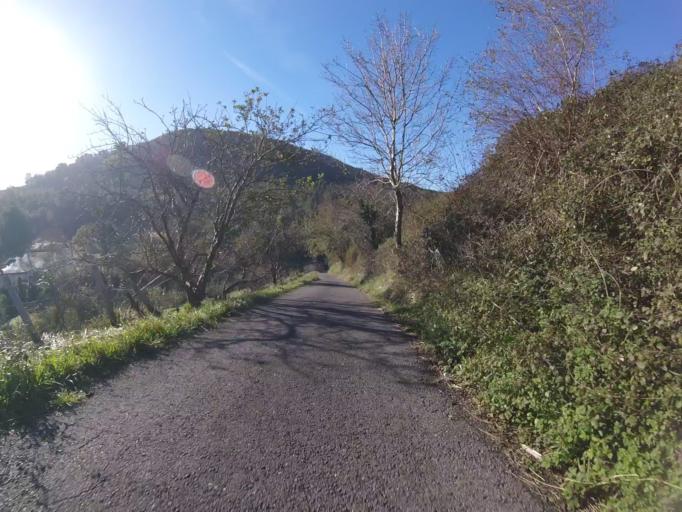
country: ES
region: Basque Country
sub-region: Provincia de Guipuzcoa
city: Usurbil
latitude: 43.2980
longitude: -2.0545
